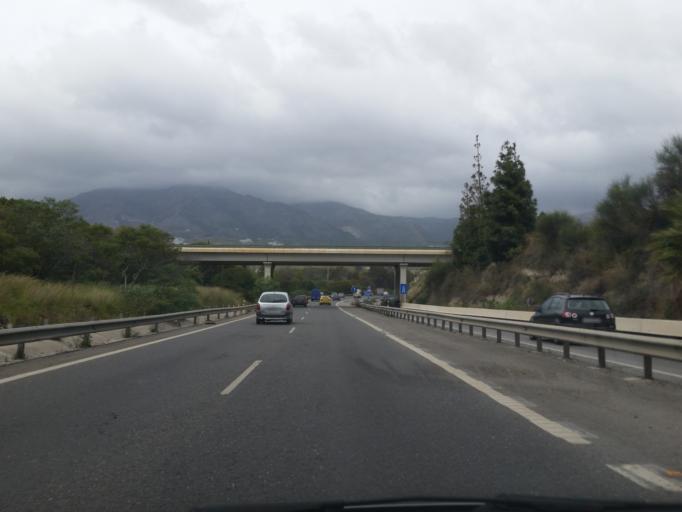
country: ES
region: Andalusia
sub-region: Provincia de Malaga
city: Fuengirola
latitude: 36.5668
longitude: -4.6224
